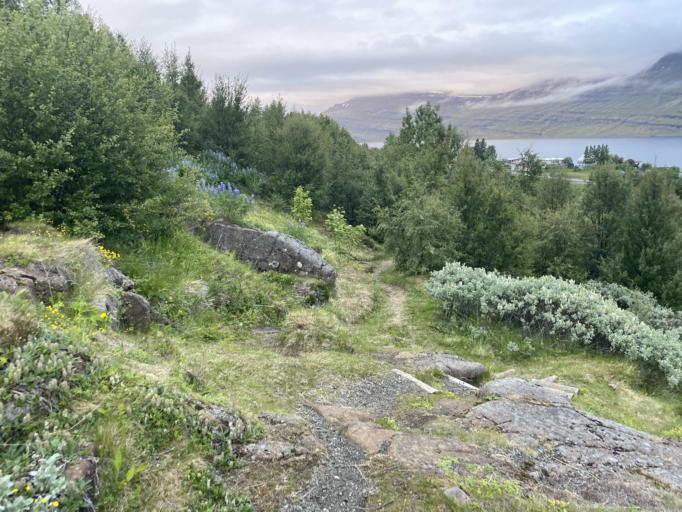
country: IS
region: East
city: Reydarfjoerdur
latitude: 65.0349
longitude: -14.2083
